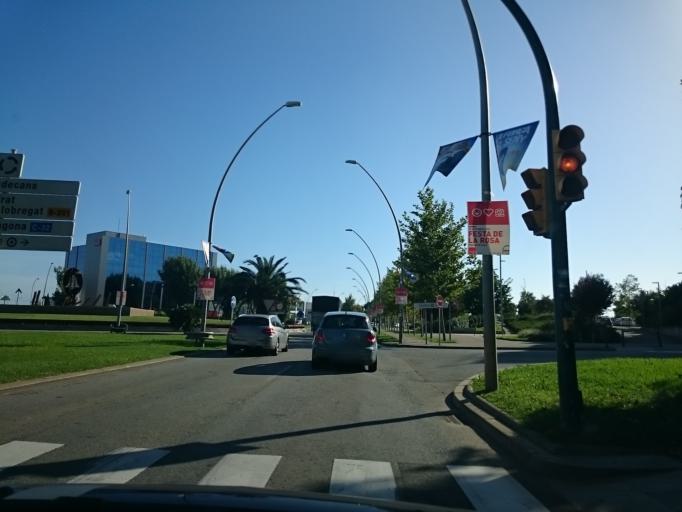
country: ES
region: Catalonia
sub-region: Provincia de Barcelona
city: Sant Boi de Llobregat
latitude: 41.3357
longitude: 2.0457
